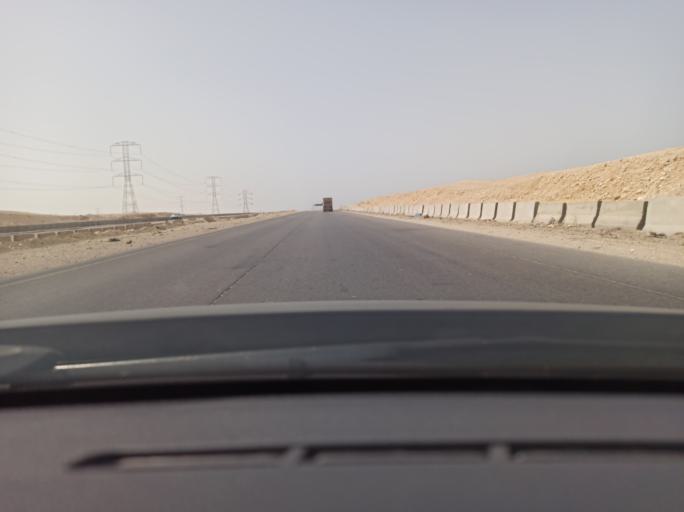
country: EG
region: Muhafazat al Fayyum
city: Al Wasitah
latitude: 29.3908
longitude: 31.3226
